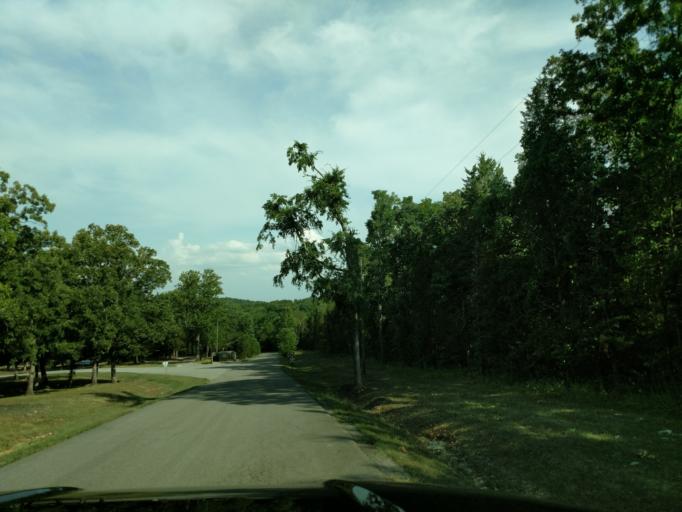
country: US
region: Missouri
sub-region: Barry County
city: Shell Knob
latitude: 36.5967
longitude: -93.5533
